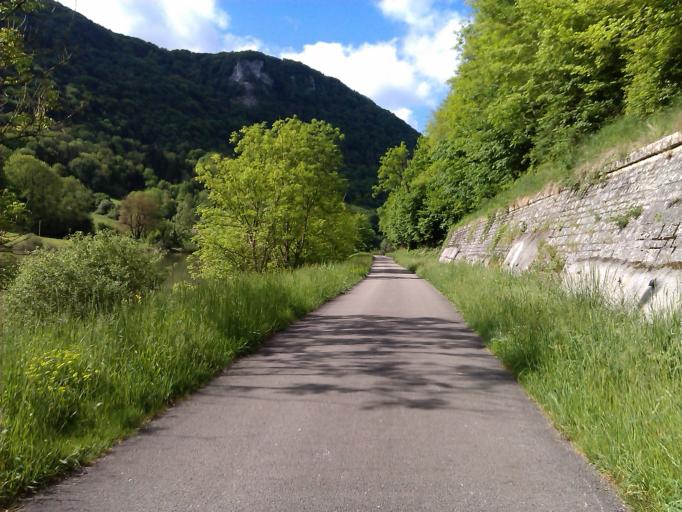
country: FR
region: Franche-Comte
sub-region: Departement du Doubs
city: Roulans
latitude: 47.3249
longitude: 6.2860
